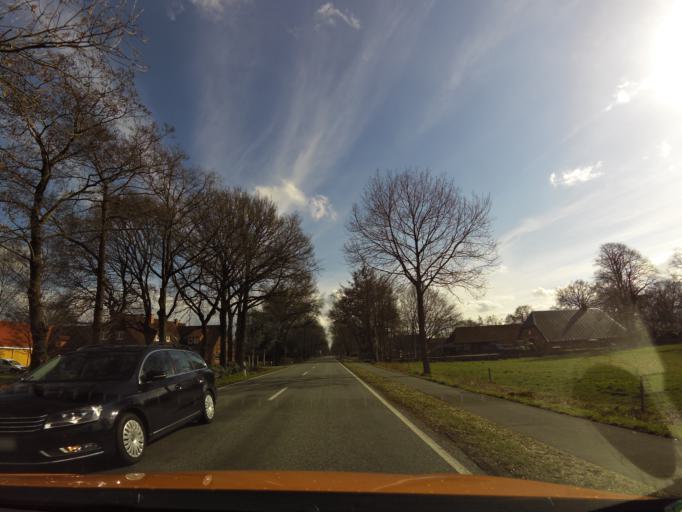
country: DE
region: Lower Saxony
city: Wardenburg
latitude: 53.0871
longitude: 8.2906
